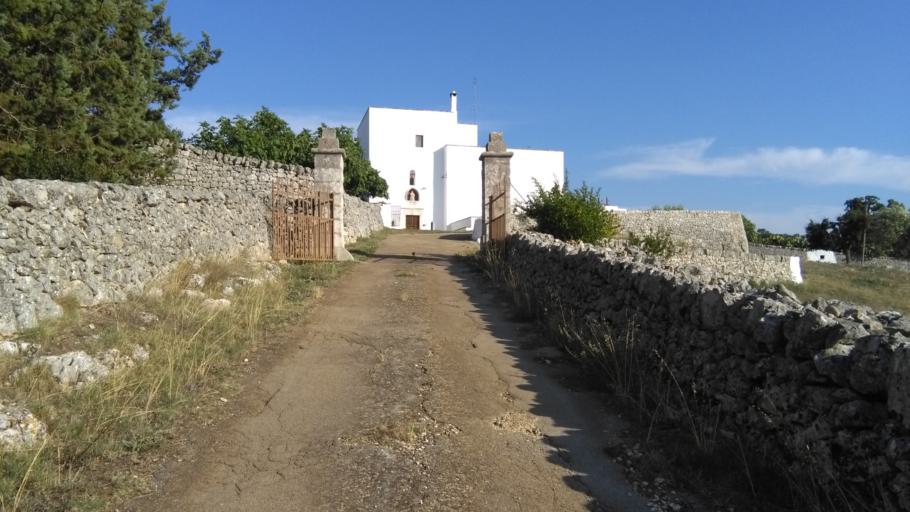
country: IT
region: Apulia
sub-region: Provincia di Bari
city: Putignano
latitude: 40.8264
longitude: 17.0629
